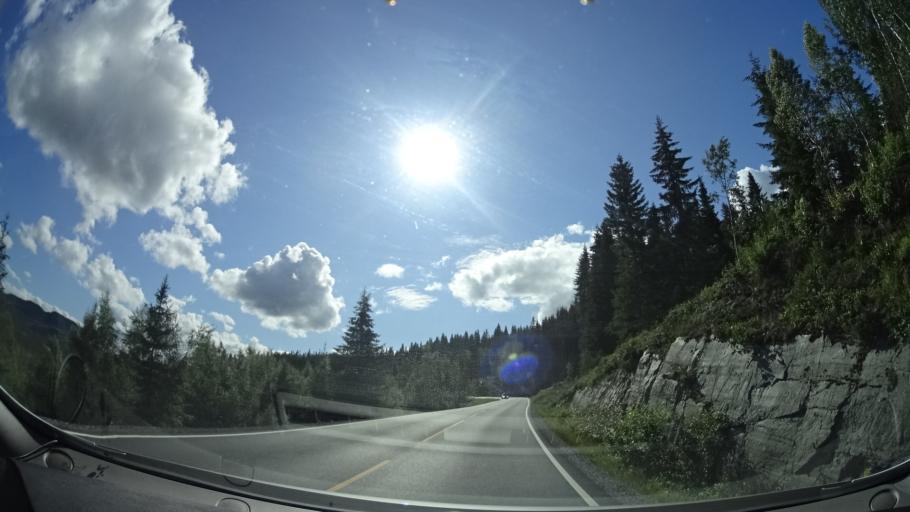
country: NO
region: Sor-Trondelag
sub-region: Snillfjord
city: Krokstadora
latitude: 63.2353
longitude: 9.5854
